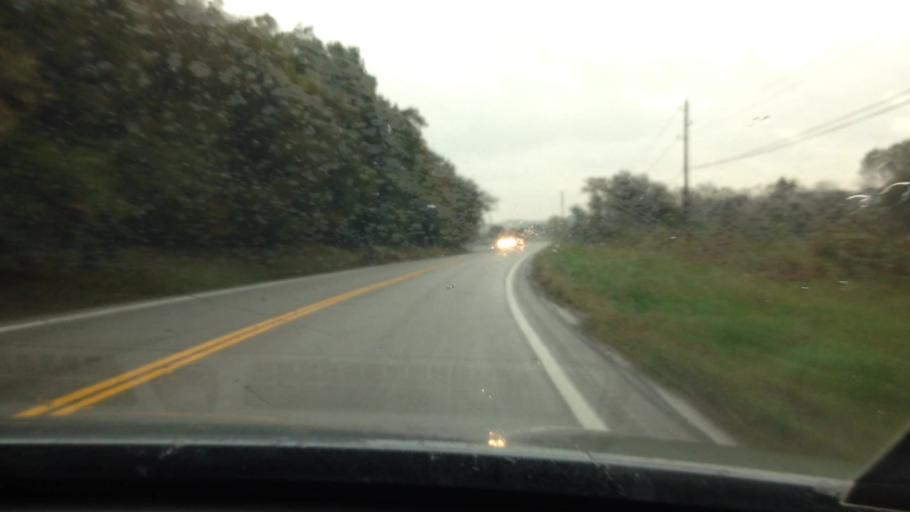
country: US
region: Missouri
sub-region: Platte County
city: Platte City
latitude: 39.3818
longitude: -94.8047
